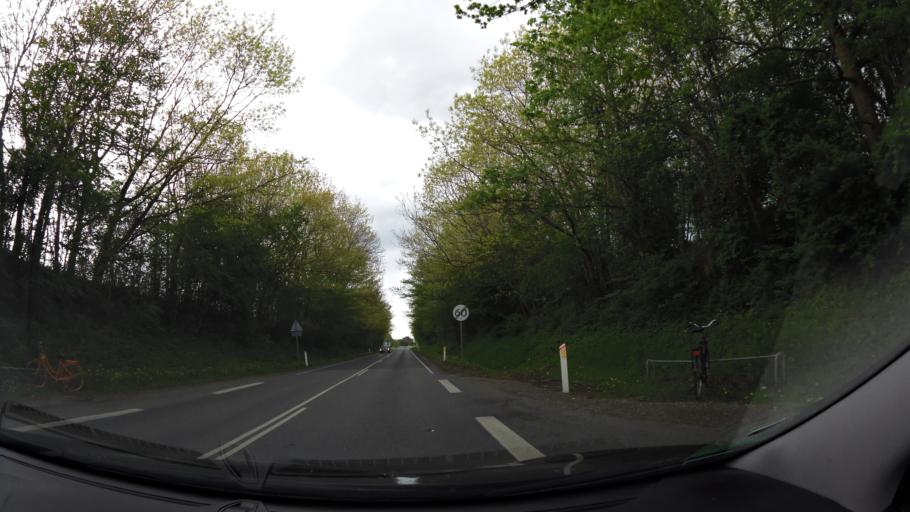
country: DK
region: South Denmark
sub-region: Nyborg Kommune
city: Nyborg
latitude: 55.2380
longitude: 10.7440
